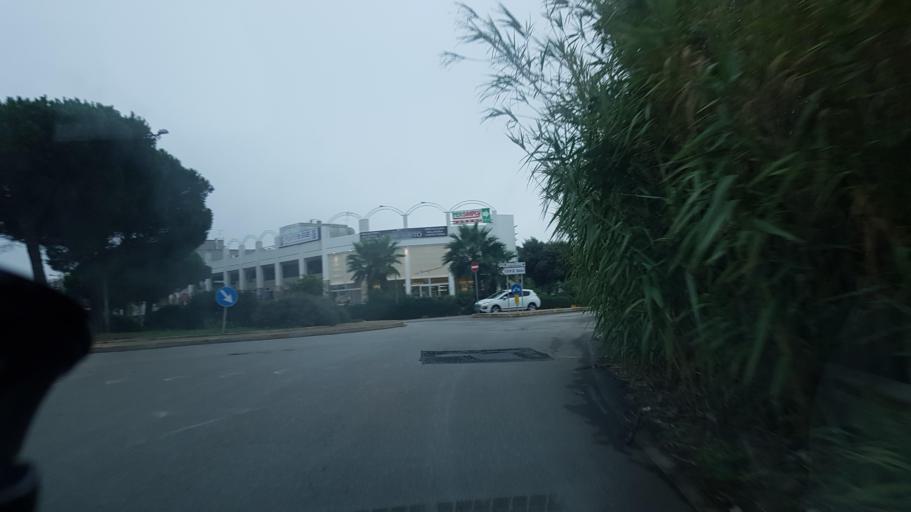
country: IT
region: Apulia
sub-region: Provincia di Brindisi
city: Ostuni
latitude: 40.7240
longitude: 17.5717
